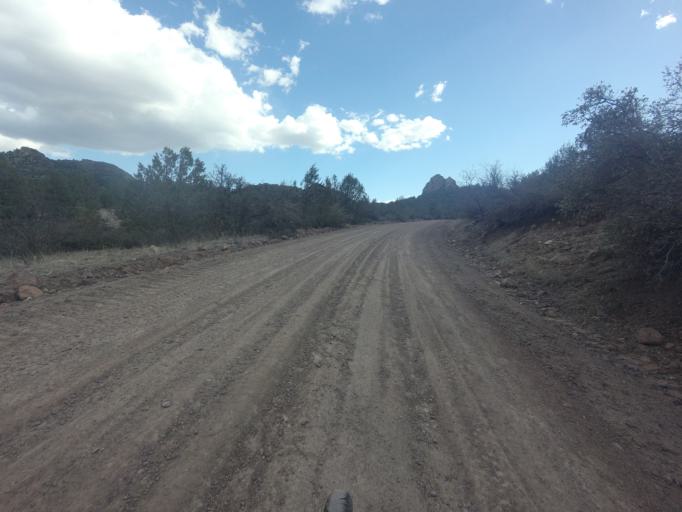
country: US
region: Arizona
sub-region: Yavapai County
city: Camp Verde
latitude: 34.4430
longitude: -111.6884
